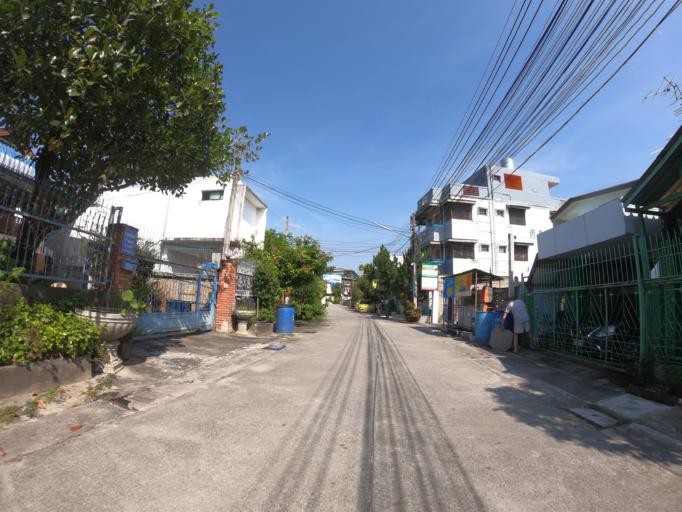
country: TH
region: Chiang Mai
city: Chiang Mai
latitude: 18.8144
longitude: 98.9878
